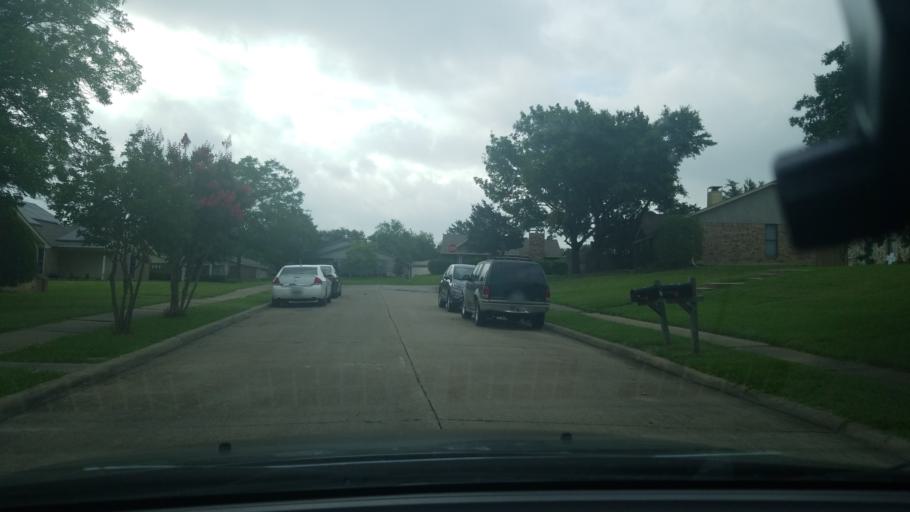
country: US
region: Texas
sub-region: Dallas County
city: Mesquite
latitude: 32.7869
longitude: -96.6431
